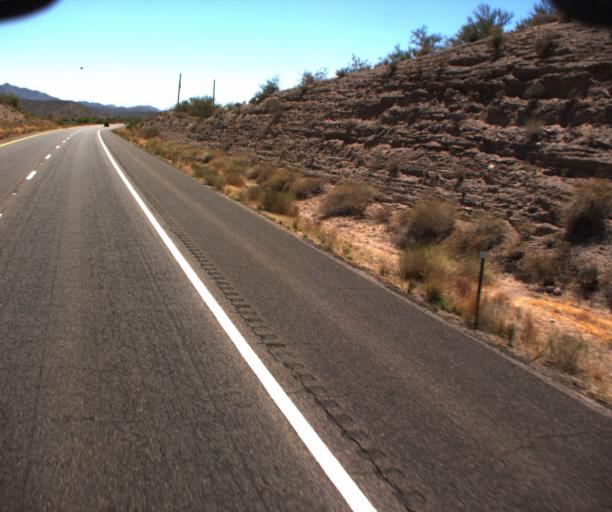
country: US
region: Arizona
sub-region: Maricopa County
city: Fountain Hills
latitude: 33.5979
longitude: -111.5903
